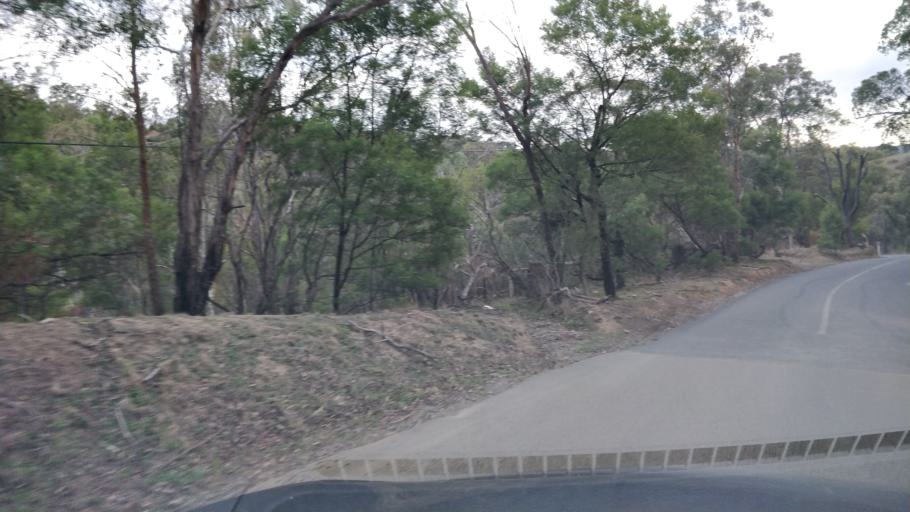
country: AU
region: Victoria
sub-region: Nillumbik
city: Research
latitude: -37.6858
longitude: 145.1800
